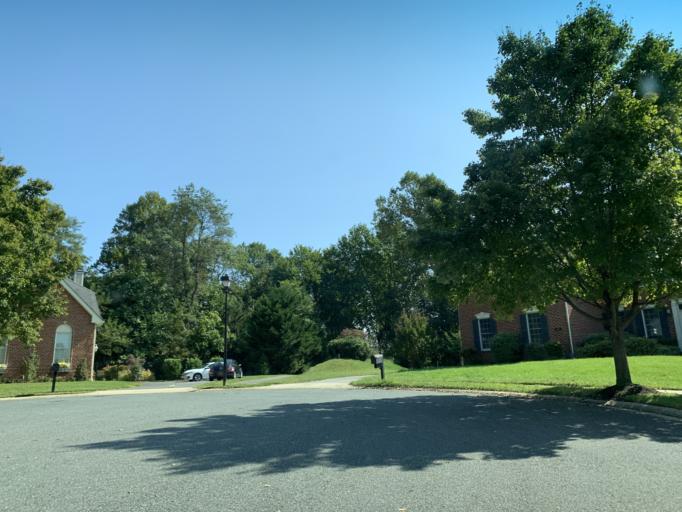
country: US
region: Maryland
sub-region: Harford County
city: Bel Air South
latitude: 39.4851
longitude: -76.3320
